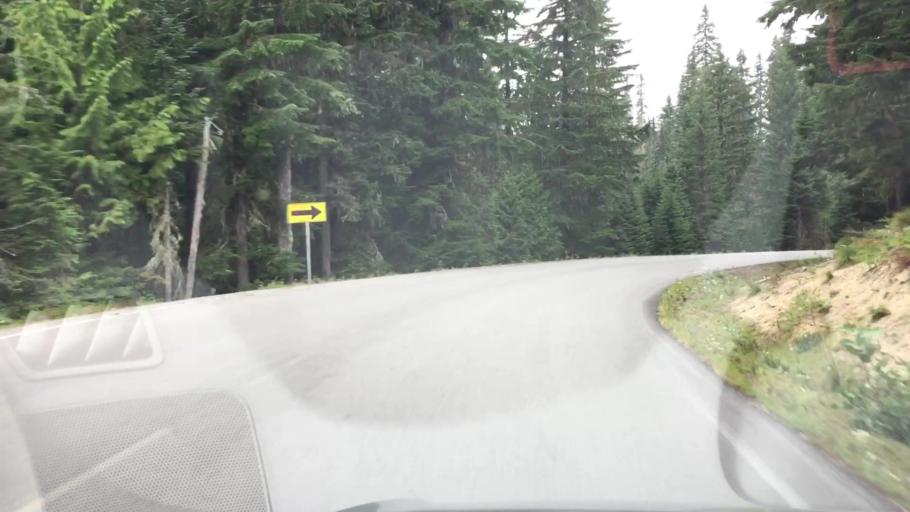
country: US
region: Washington
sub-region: Klickitat County
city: White Salmon
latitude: 46.1835
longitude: -121.6427
